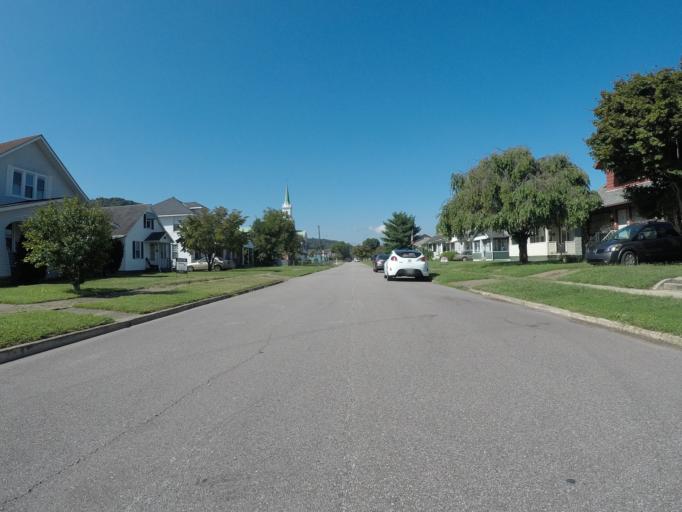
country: US
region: Ohio
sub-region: Lawrence County
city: Burlington
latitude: 38.4008
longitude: -82.5038
